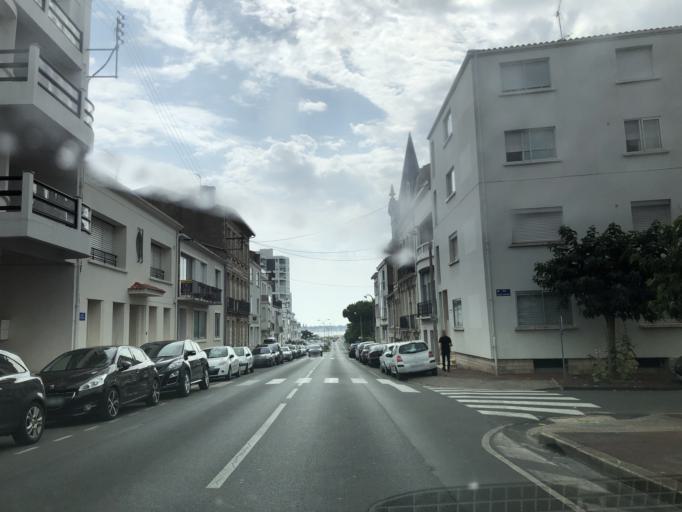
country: FR
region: Poitou-Charentes
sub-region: Departement de la Charente-Maritime
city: Royan
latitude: 45.6210
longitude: -1.0369
